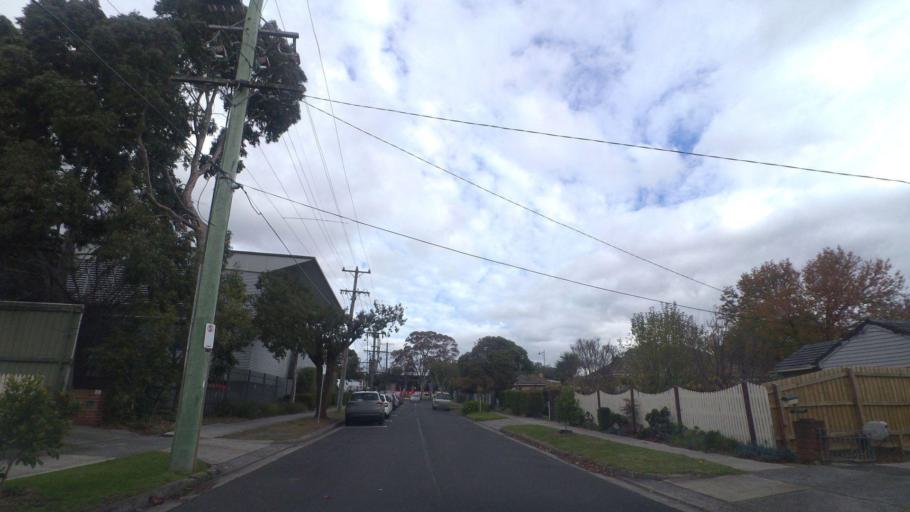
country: AU
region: Victoria
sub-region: Whitehorse
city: Nunawading
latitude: -37.8172
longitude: 145.1664
